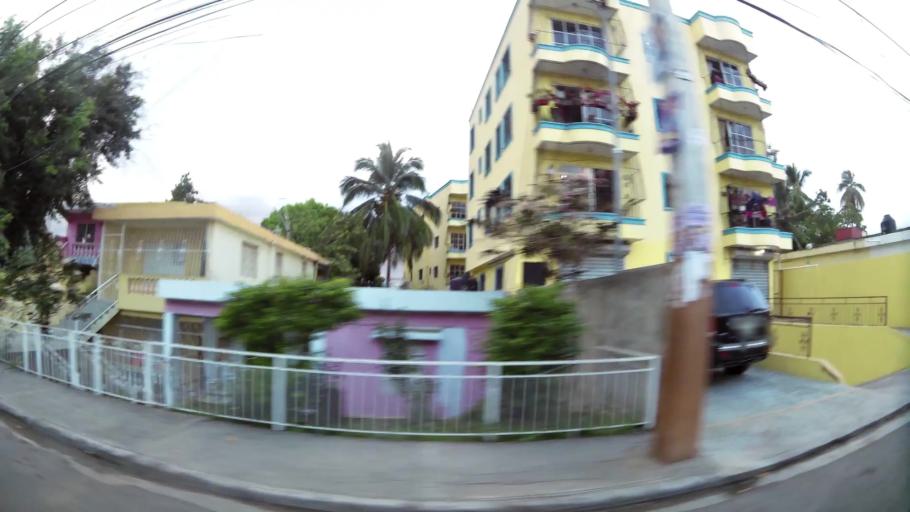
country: DO
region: Santo Domingo
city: Santo Domingo Oeste
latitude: 18.5245
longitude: -70.0149
